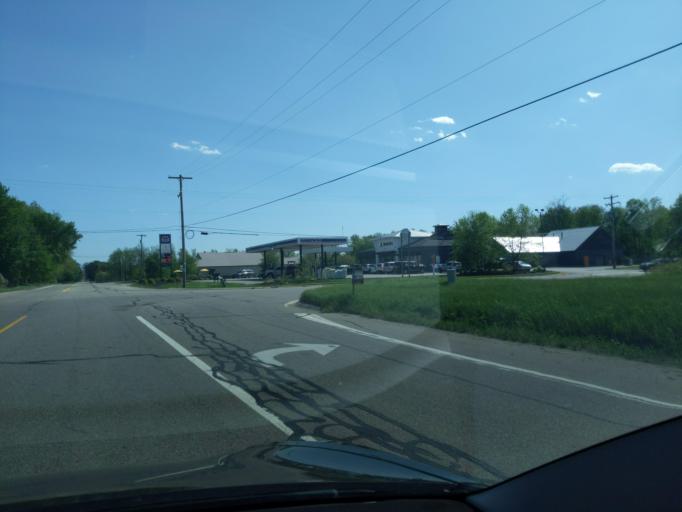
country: US
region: Michigan
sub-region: Kent County
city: Lowell
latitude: 42.8492
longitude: -85.3704
